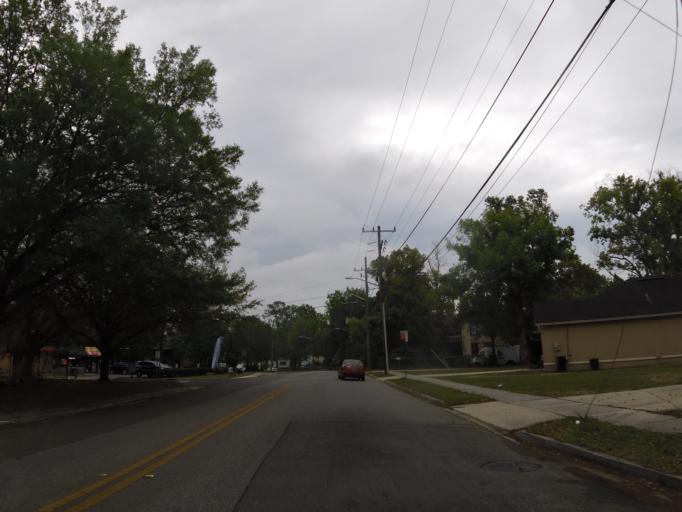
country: US
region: Florida
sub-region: Duval County
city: Jacksonville
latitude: 30.2976
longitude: -81.6311
